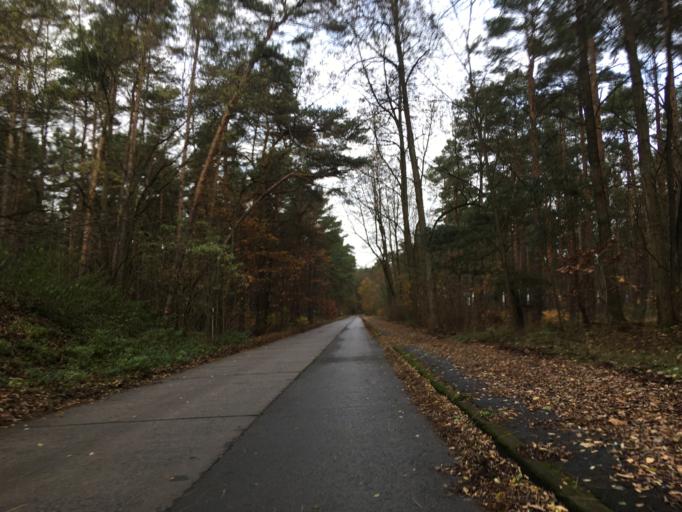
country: DE
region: Brandenburg
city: Schenkendobern
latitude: 51.9697
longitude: 14.5338
